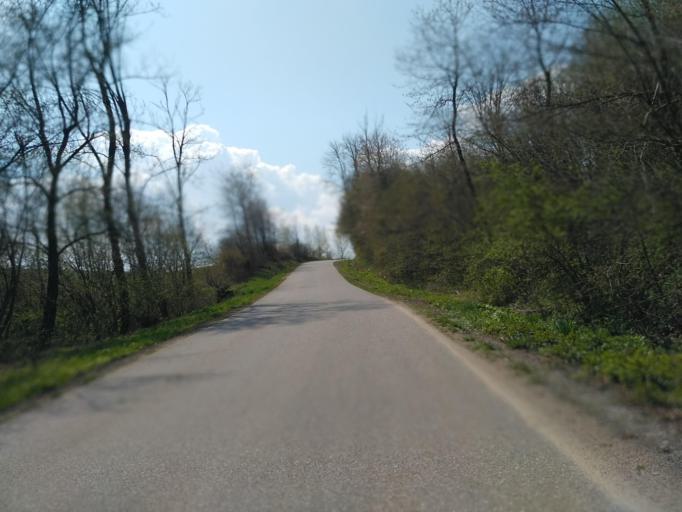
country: PL
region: Subcarpathian Voivodeship
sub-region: Powiat sanocki
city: Zarszyn
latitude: 49.5535
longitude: 21.9897
